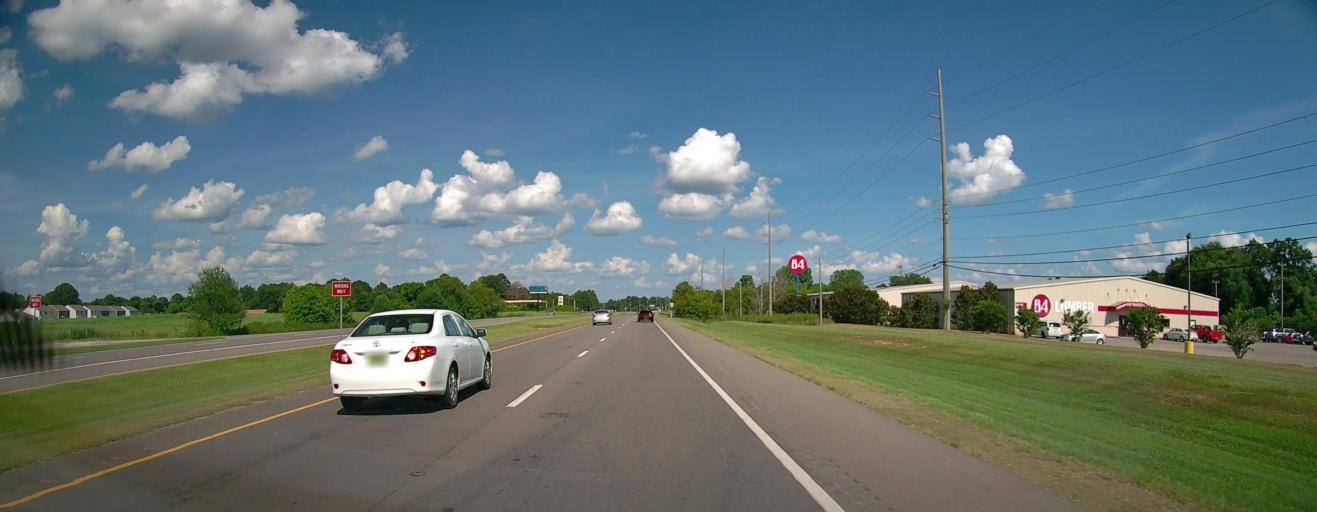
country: US
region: Alabama
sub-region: Tuscaloosa County
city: Northport
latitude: 33.2336
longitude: -87.6346
